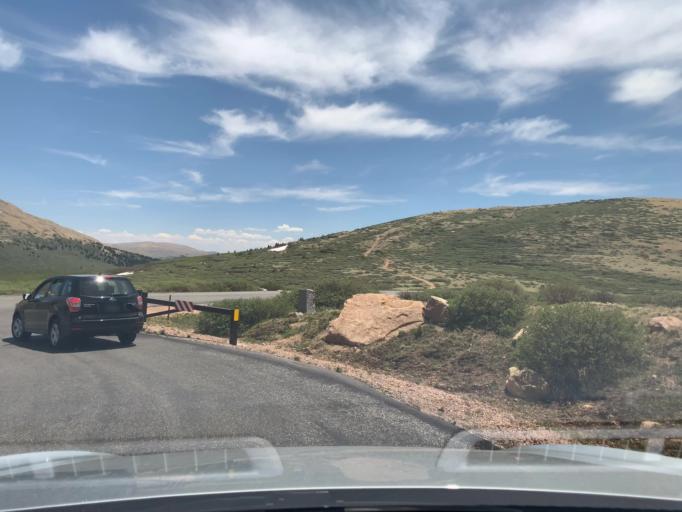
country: US
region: Colorado
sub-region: Clear Creek County
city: Georgetown
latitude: 39.5955
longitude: -105.7111
